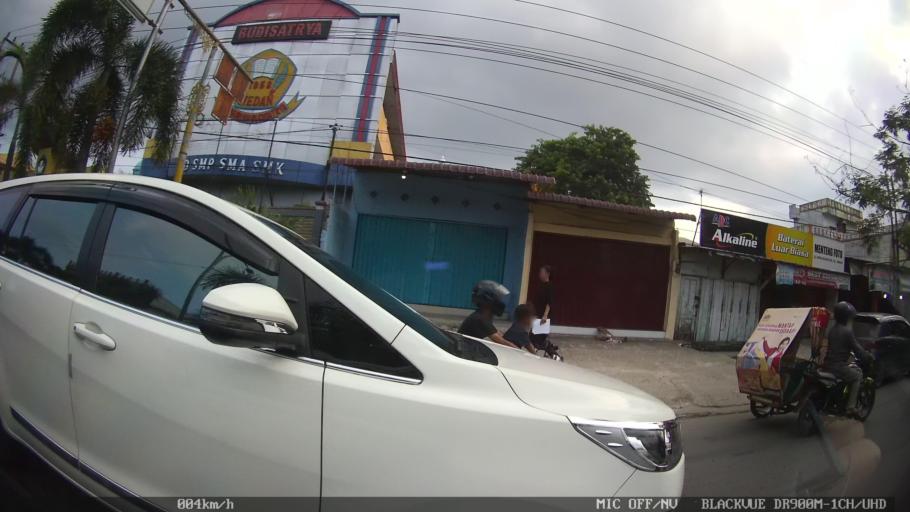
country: ID
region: North Sumatra
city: Medan
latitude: 3.5972
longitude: 98.7220
